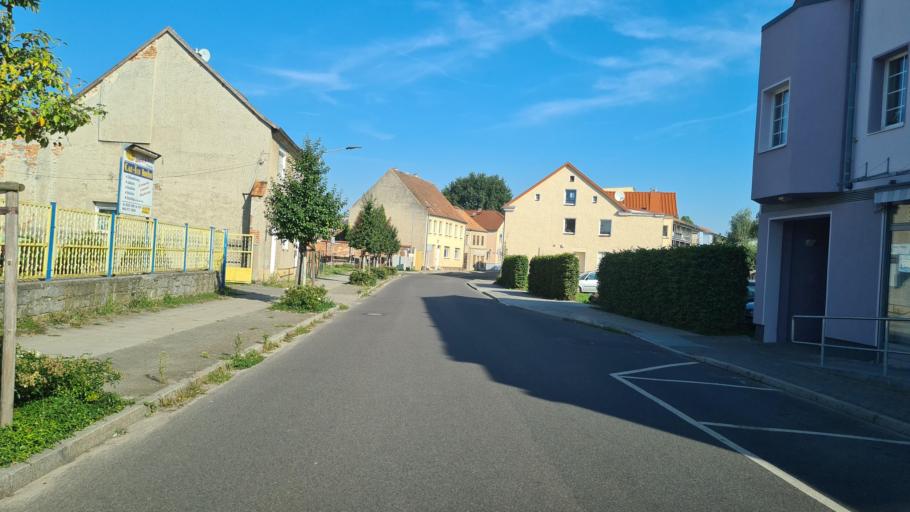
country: DE
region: Brandenburg
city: Friesack
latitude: 52.7399
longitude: 12.5790
